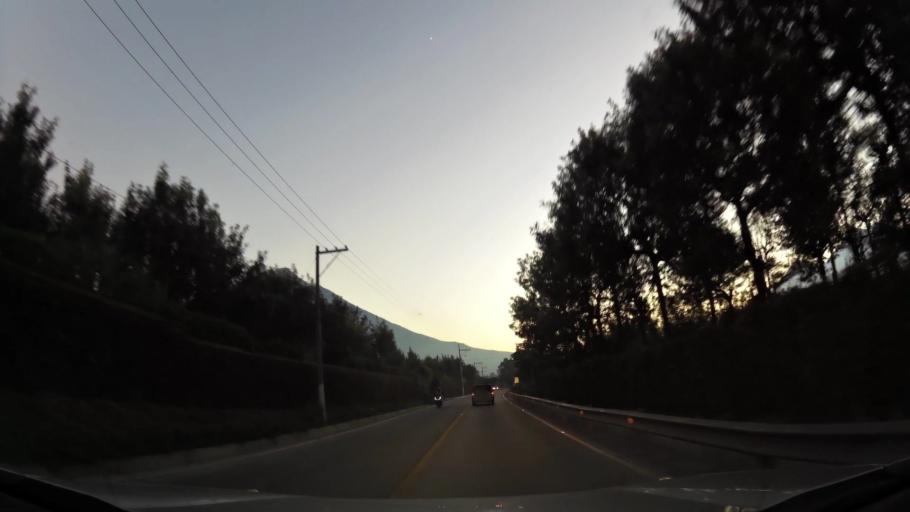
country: GT
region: Sacatepequez
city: Ciudad Vieja
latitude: 14.5390
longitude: -90.7476
